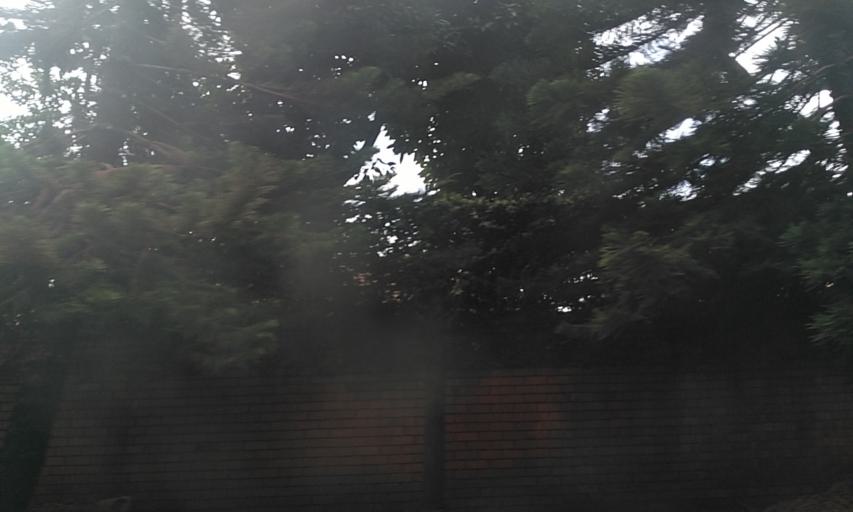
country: UG
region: Central Region
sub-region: Kampala District
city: Kampala
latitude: 0.3250
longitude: 32.5943
